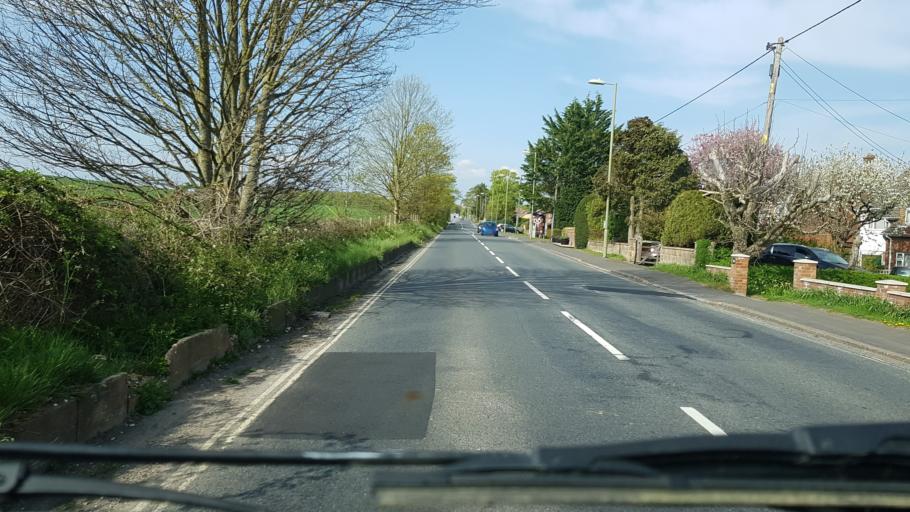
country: GB
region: England
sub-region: Hampshire
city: Basingstoke
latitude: 51.2713
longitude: -1.1295
